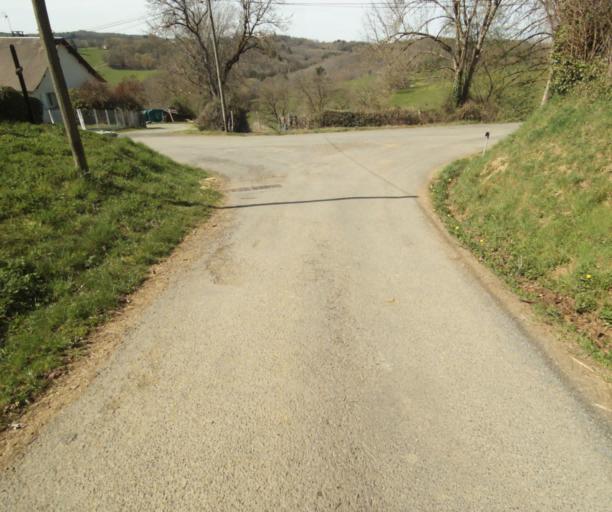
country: FR
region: Limousin
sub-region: Departement de la Correze
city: Seilhac
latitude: 45.3872
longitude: 1.7813
